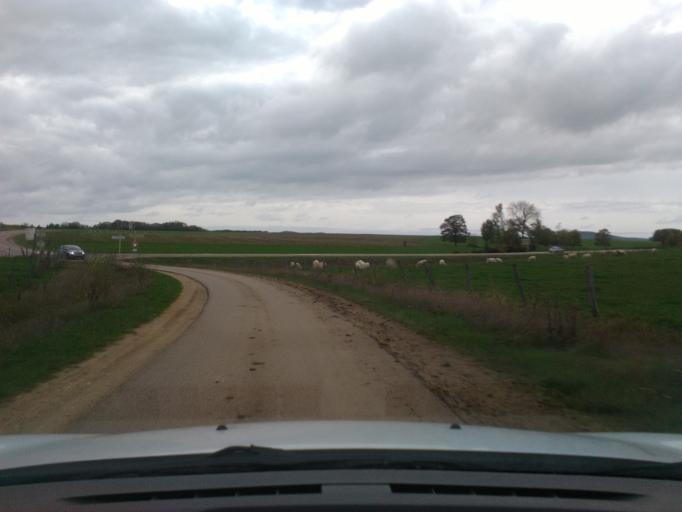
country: FR
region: Lorraine
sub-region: Departement des Vosges
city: Mirecourt
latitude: 48.3392
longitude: 6.1184
